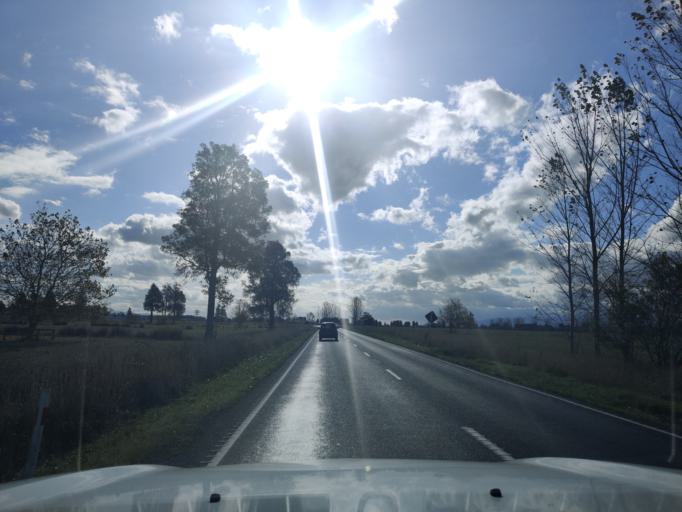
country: NZ
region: Waikato
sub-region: Hauraki District
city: Ngatea
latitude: -37.3082
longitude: 175.5640
